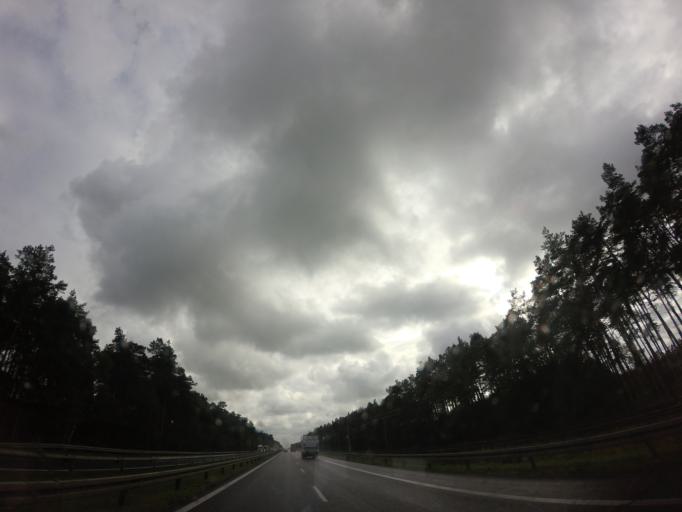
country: PL
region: West Pomeranian Voivodeship
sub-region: Powiat goleniowski
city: Goleniow
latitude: 53.5168
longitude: 14.8048
